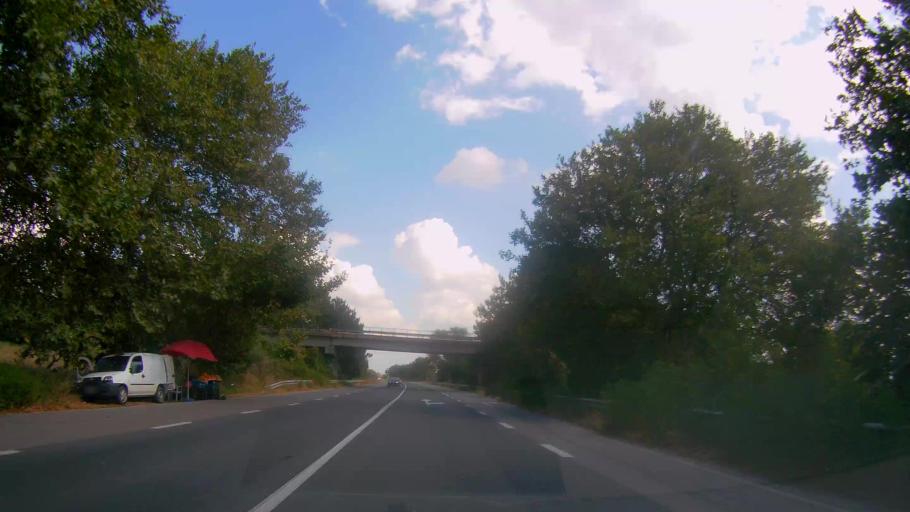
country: BG
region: Sliven
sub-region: Obshtina Sliven
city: Kermen
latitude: 42.6312
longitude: 26.1781
